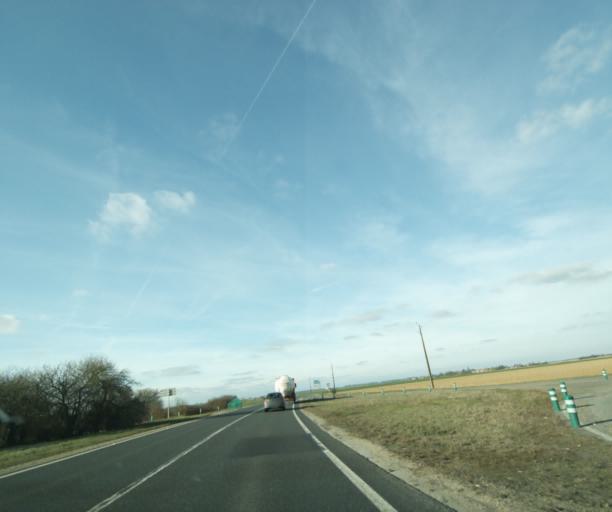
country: FR
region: Ile-de-France
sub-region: Departement des Yvelines
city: Ablis
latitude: 48.4806
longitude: 1.8494
